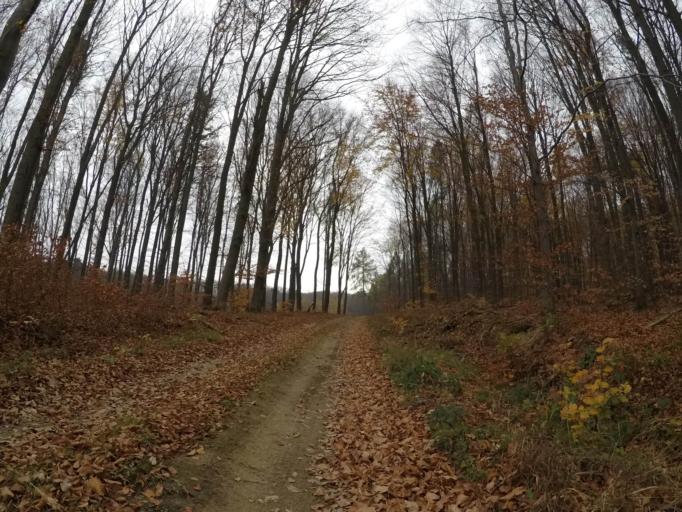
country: SK
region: Presovsky
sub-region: Okres Presov
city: Presov
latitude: 48.8897
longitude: 21.1715
